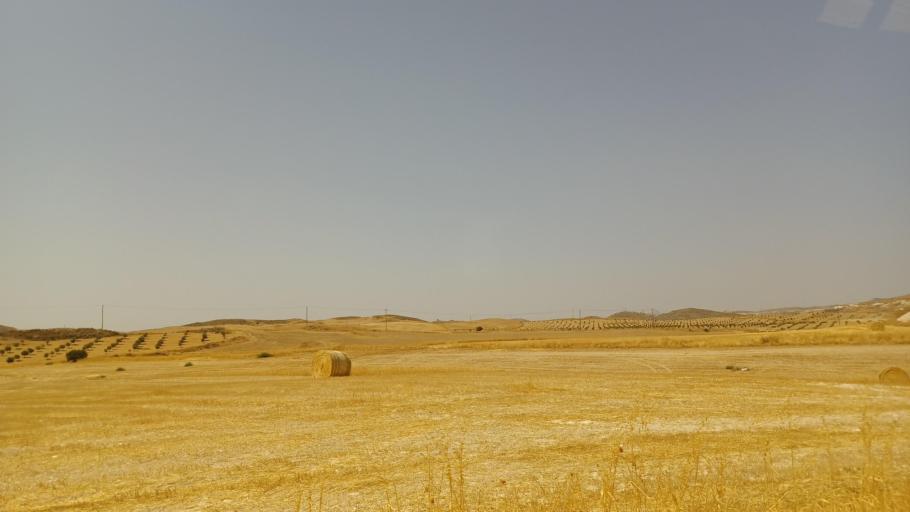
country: CY
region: Larnaka
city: Troulloi
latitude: 35.0311
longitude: 33.5906
